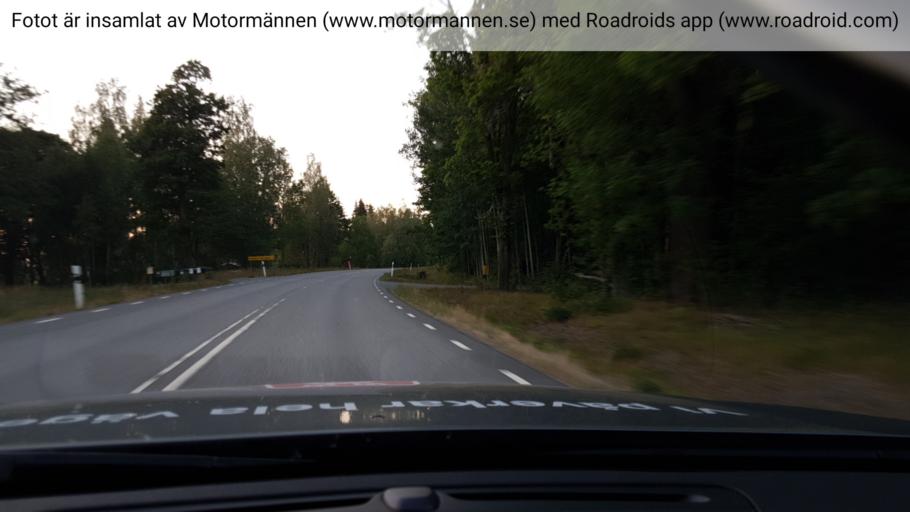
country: SE
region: Uppsala
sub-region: Heby Kommun
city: OEstervala
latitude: 60.1498
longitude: 17.1996
